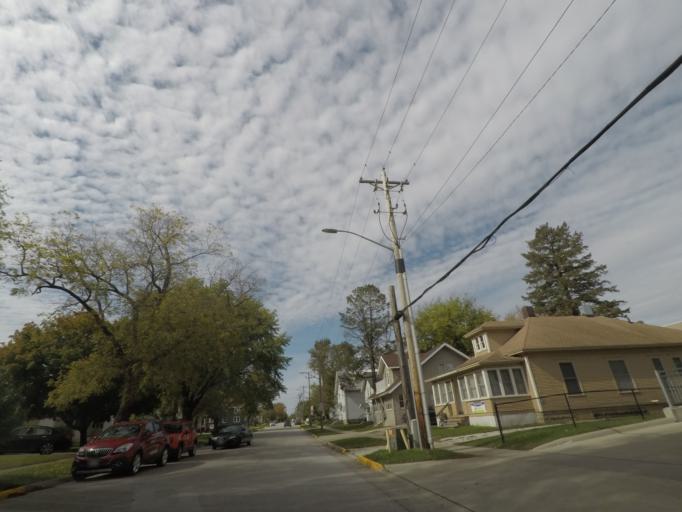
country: US
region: Iowa
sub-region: Story County
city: Ames
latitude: 42.0192
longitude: -93.6471
